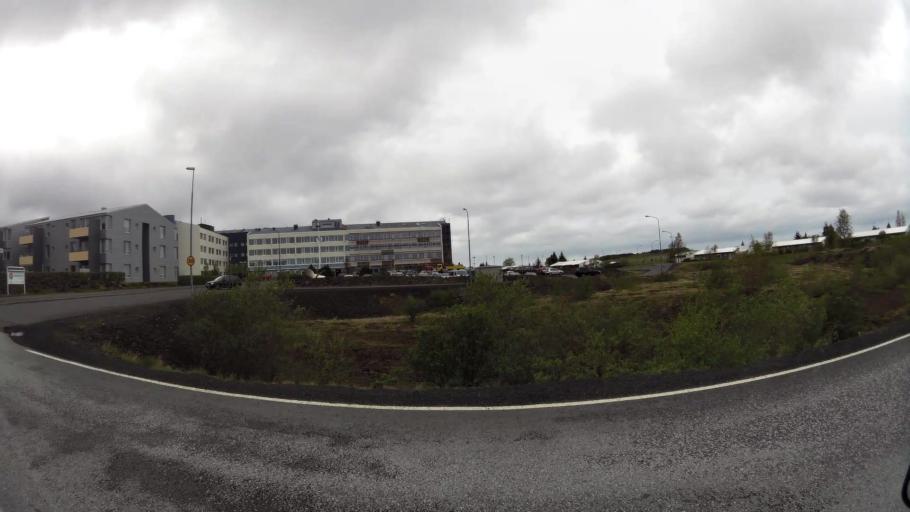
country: IS
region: Capital Region
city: Hafnarfjoerdur
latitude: 64.0801
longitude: -21.9711
